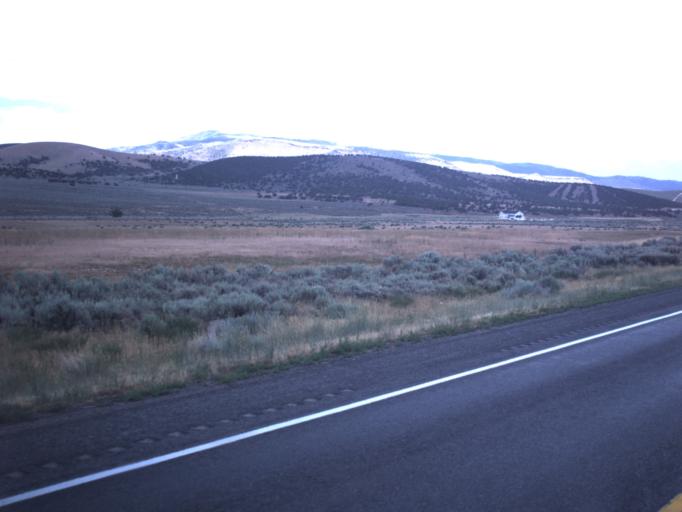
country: US
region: Utah
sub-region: Sanpete County
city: Fountain Green
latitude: 39.6508
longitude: -111.6480
